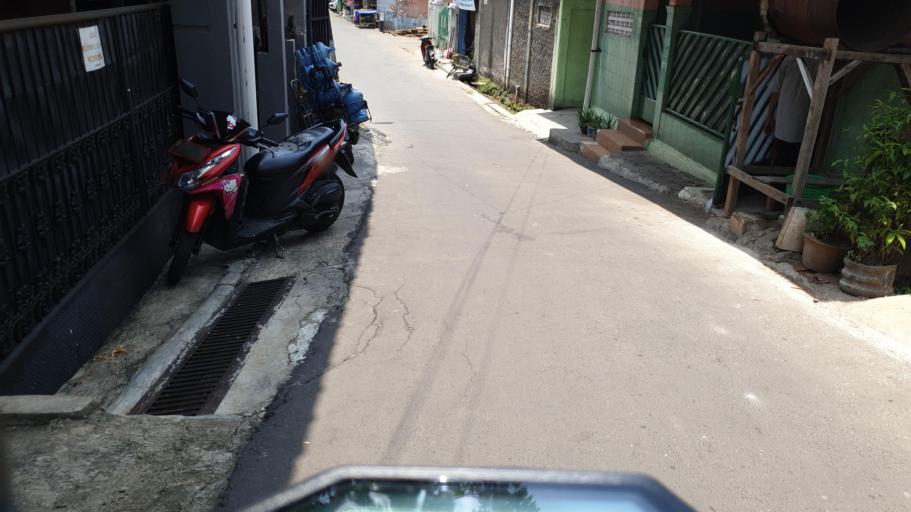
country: ID
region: West Java
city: Depok
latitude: -6.3288
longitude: 106.8307
